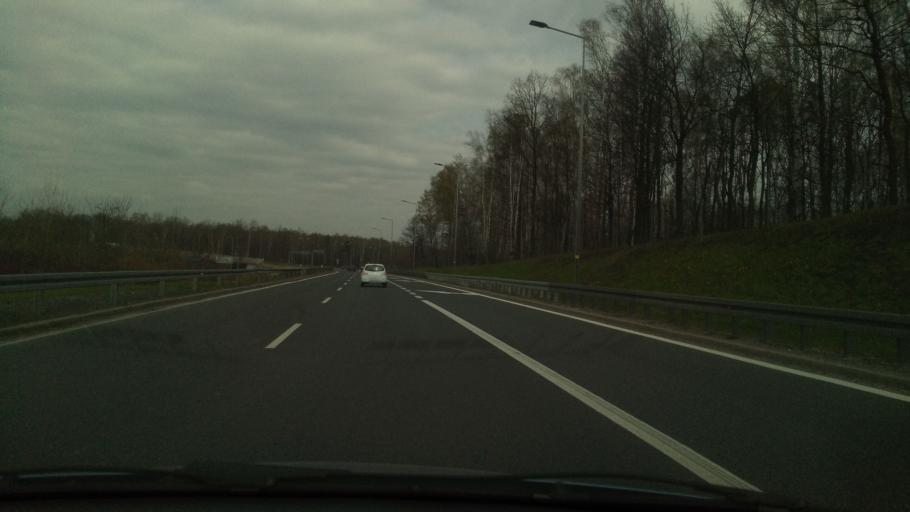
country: PL
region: Silesian Voivodeship
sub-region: Katowice
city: Katowice
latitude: 50.2426
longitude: 19.0537
